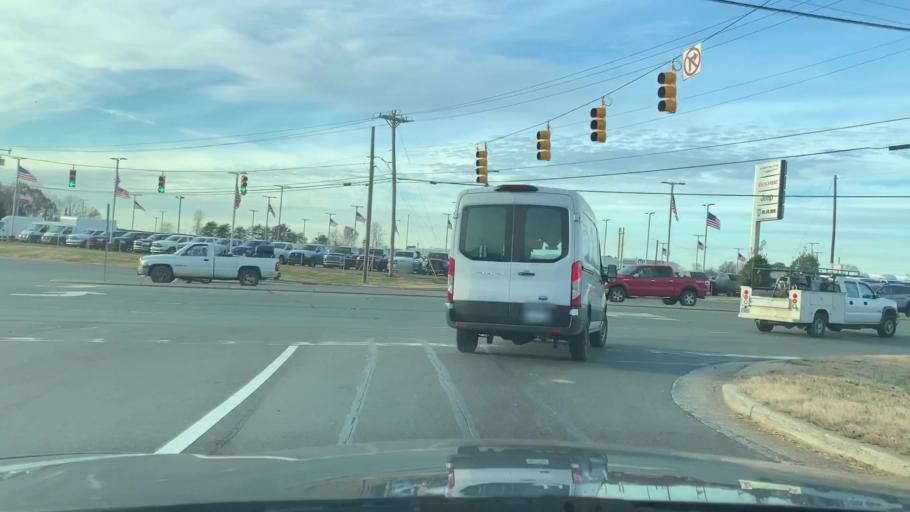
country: US
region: North Carolina
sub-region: Alamance County
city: Graham
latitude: 36.0648
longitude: -79.4304
